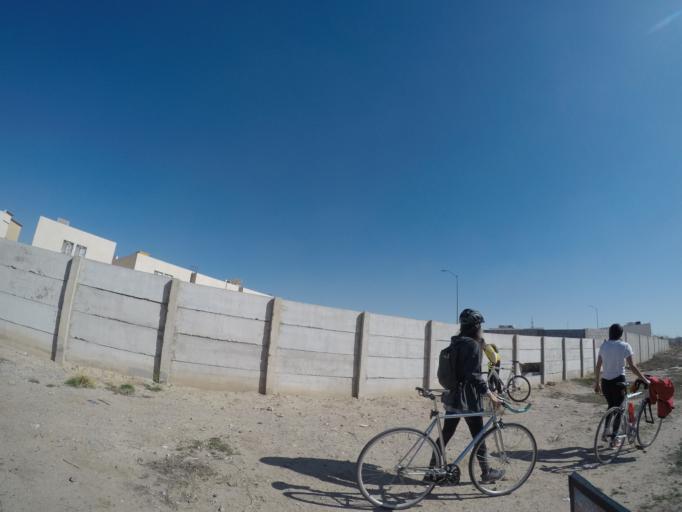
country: US
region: Texas
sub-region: El Paso County
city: Socorro
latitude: 31.6628
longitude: -106.3768
